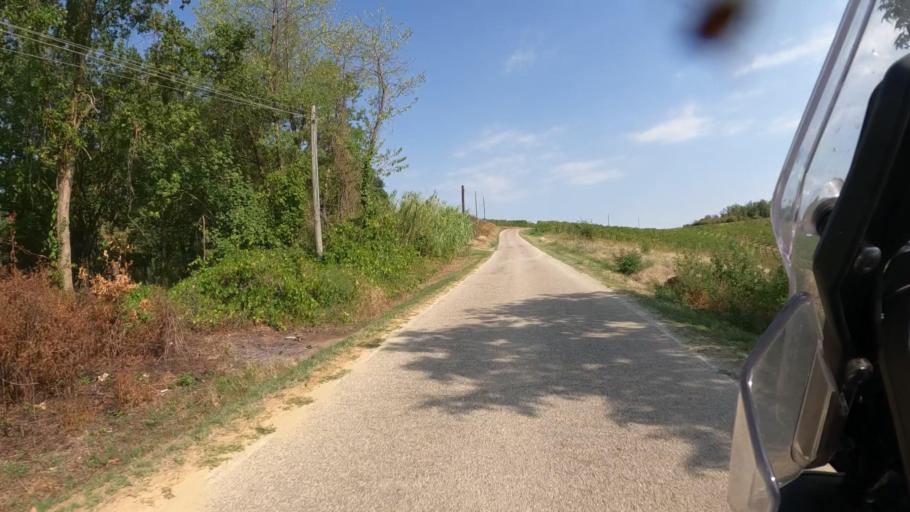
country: IT
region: Piedmont
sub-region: Provincia di Asti
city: Viarigi
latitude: 44.9557
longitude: 8.3736
